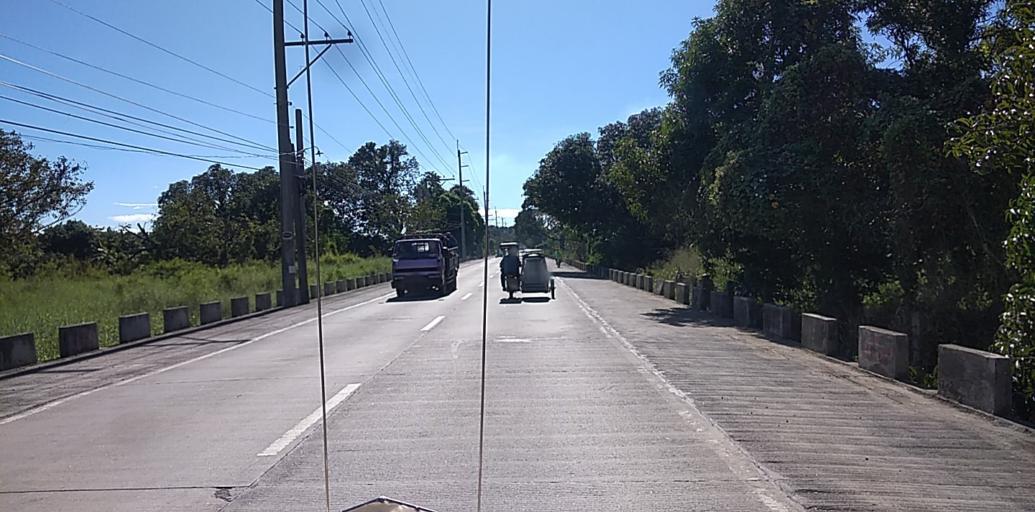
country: PH
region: Central Luzon
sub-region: Province of Pampanga
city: Santo Domingo
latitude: 15.0704
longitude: 120.7635
